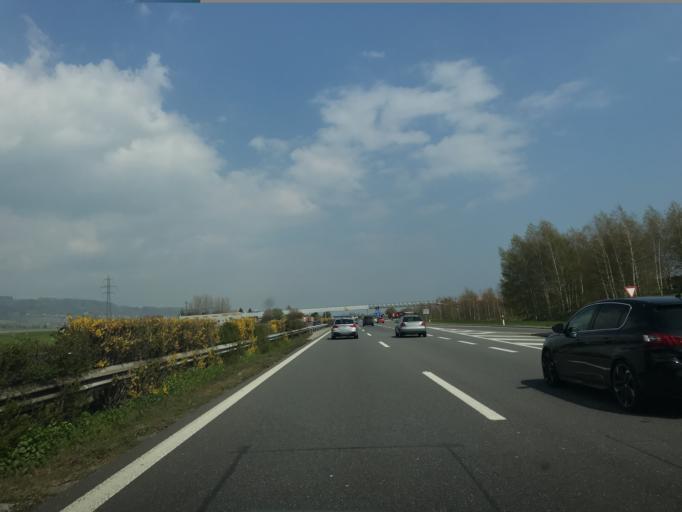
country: CH
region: Vaud
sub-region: Nyon District
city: Gland
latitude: 46.4437
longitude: 6.2926
